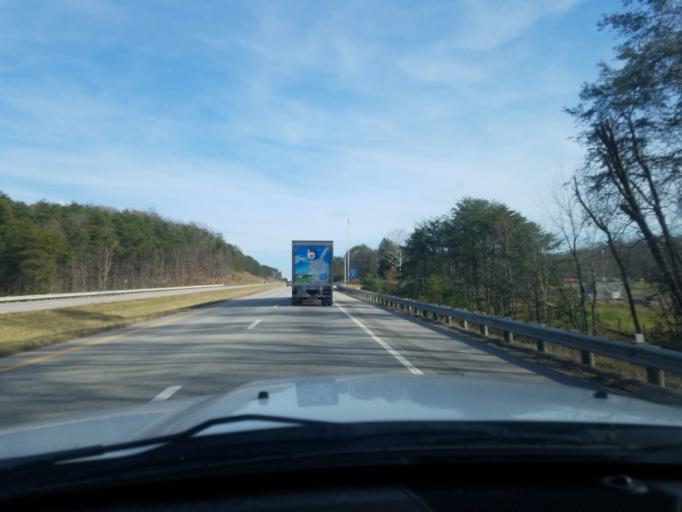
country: US
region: West Virginia
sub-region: Wood County
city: Washington
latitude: 39.2364
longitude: -81.7654
